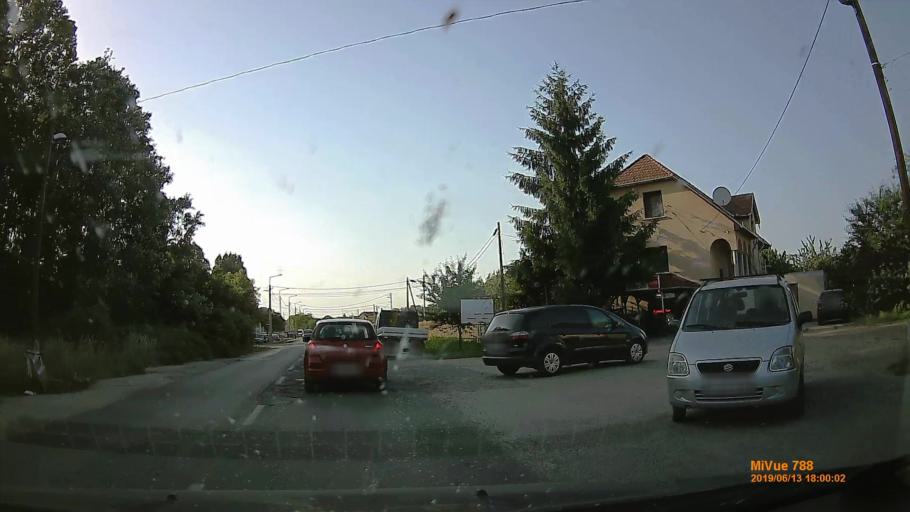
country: HU
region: Pest
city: Ecser
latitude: 47.4458
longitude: 19.3104
